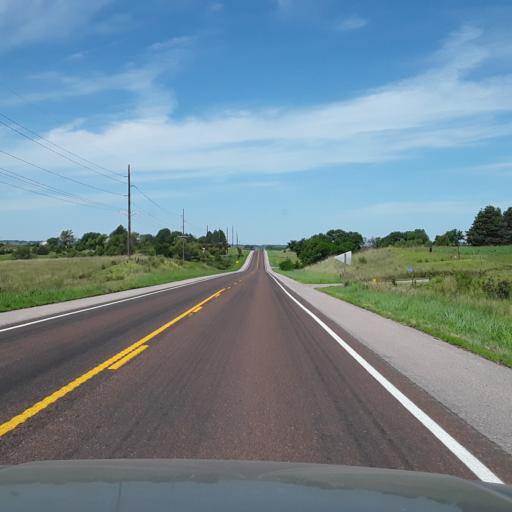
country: US
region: Nebraska
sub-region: Seward County
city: Milford
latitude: 40.8865
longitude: -96.8925
